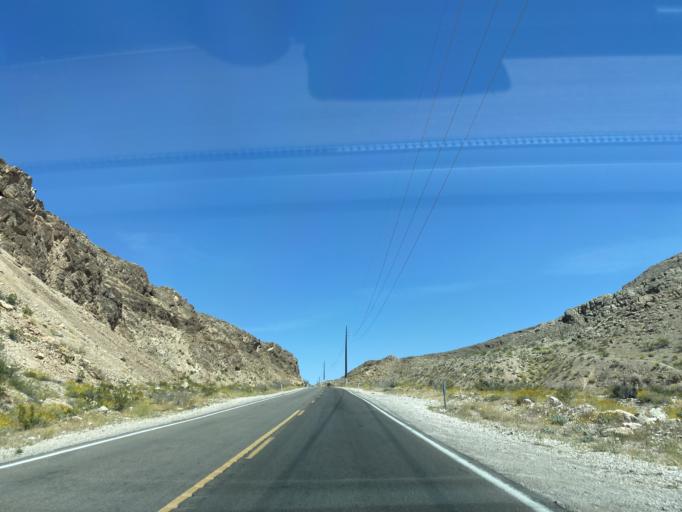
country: US
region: Nevada
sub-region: Clark County
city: Nellis Air Force Base
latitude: 36.1995
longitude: -115.0002
